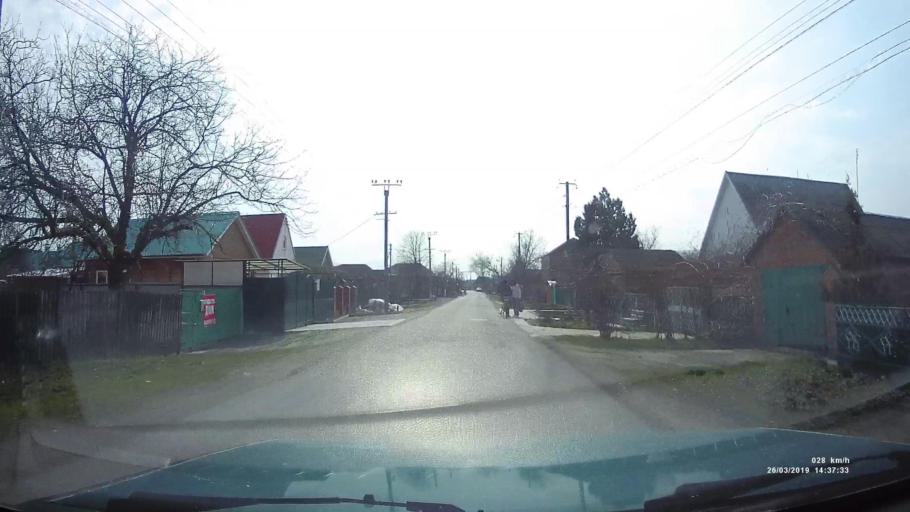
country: RU
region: Rostov
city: Novobessergenovka
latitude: 47.1841
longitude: 38.8658
